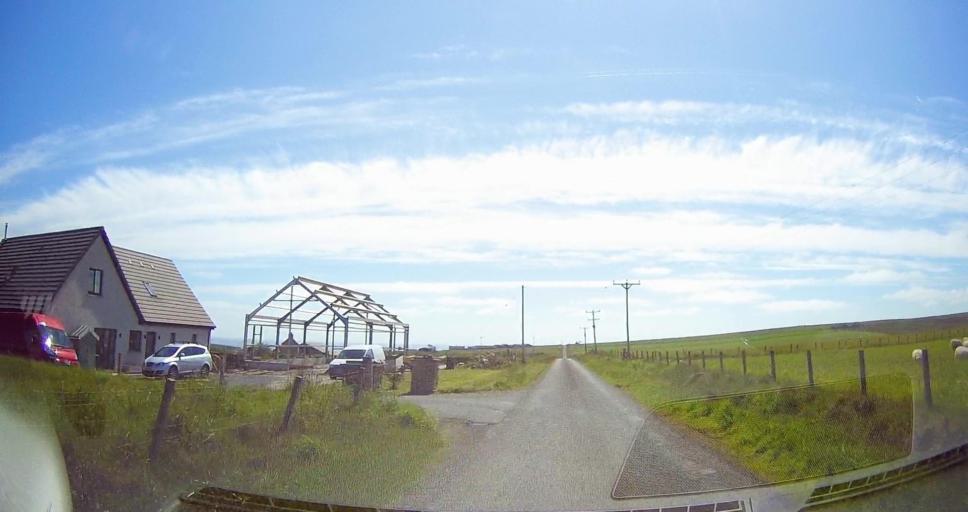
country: GB
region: Scotland
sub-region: Orkney Islands
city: Kirkwall
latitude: 58.8271
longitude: -2.9114
